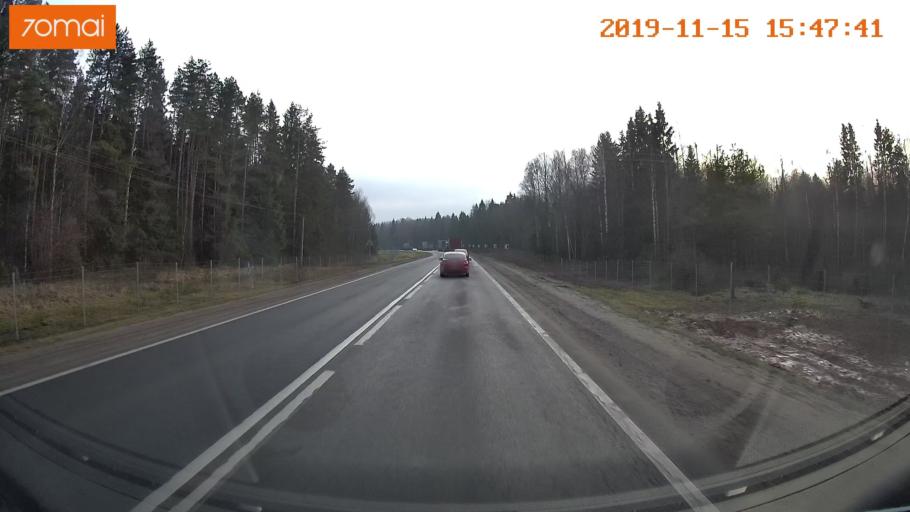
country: RU
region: Jaroslavl
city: Danilov
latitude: 57.9356
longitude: 40.0078
